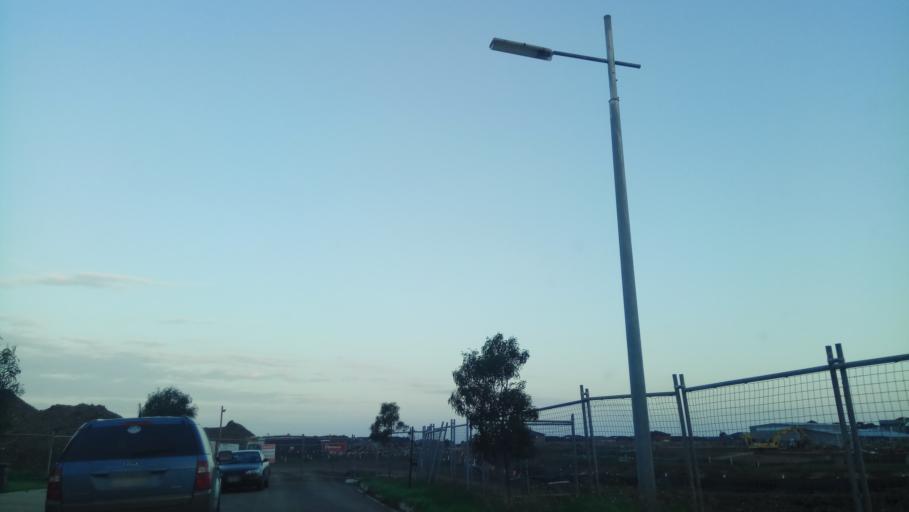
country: AU
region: Victoria
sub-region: Wyndham
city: Point Cook
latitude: -37.9122
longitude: 144.7666
